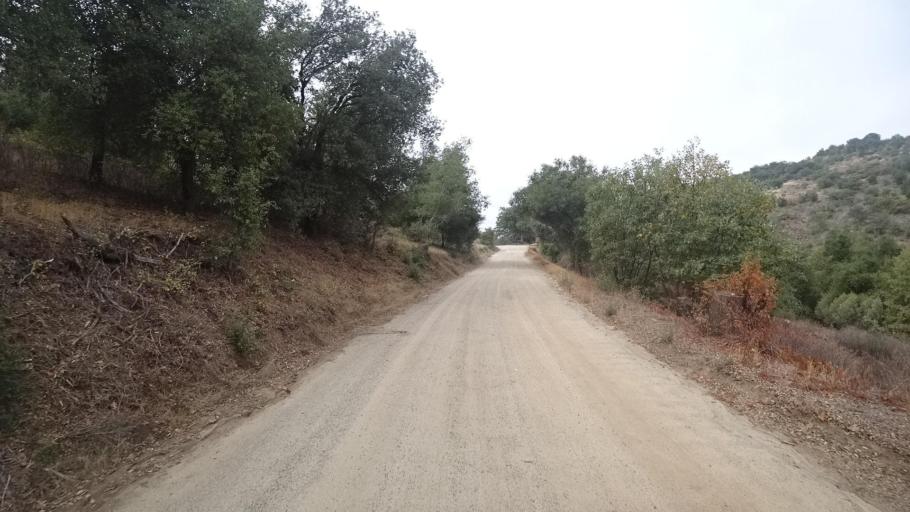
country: US
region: California
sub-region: San Diego County
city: Julian
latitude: 33.0330
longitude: -116.6547
